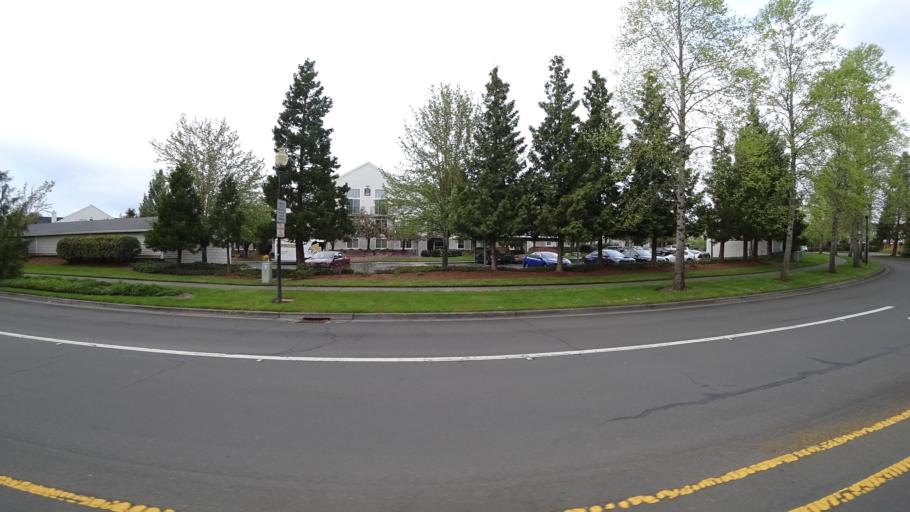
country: US
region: Oregon
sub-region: Washington County
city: Hillsboro
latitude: 45.5426
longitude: -122.9696
